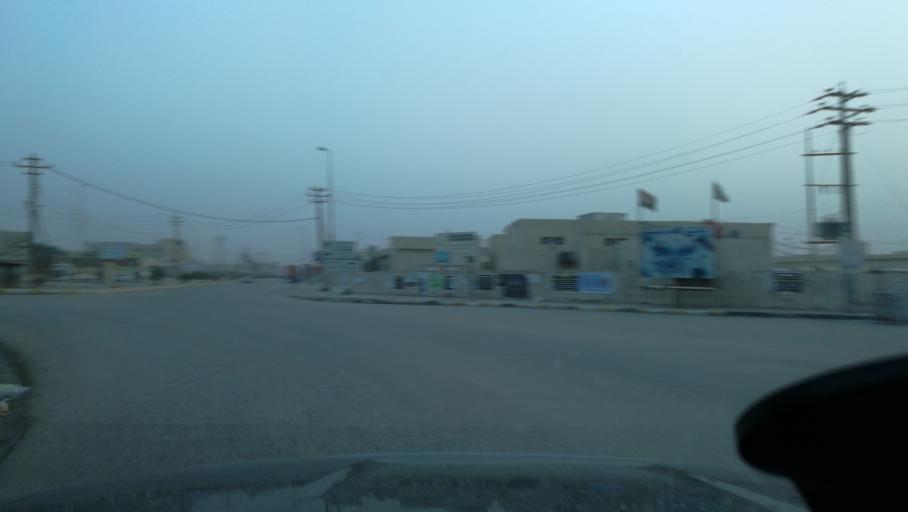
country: IQ
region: Dhi Qar
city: An Nasiriyah
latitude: 31.0373
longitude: 46.2394
